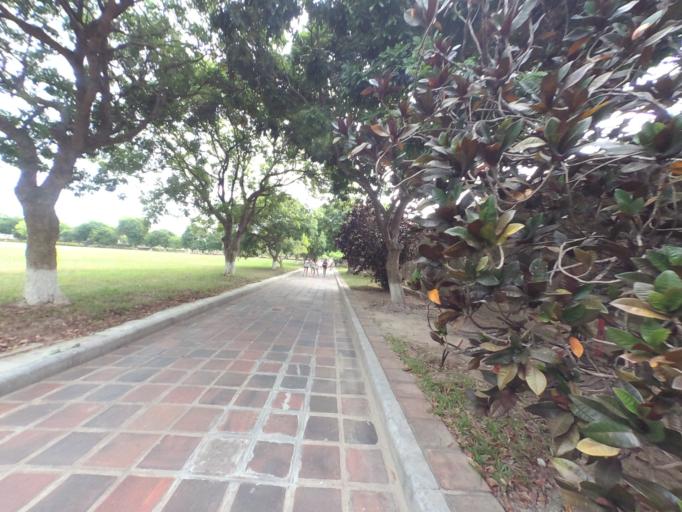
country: VN
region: Thua Thien-Hue
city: Hue
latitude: 16.4669
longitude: 107.5779
